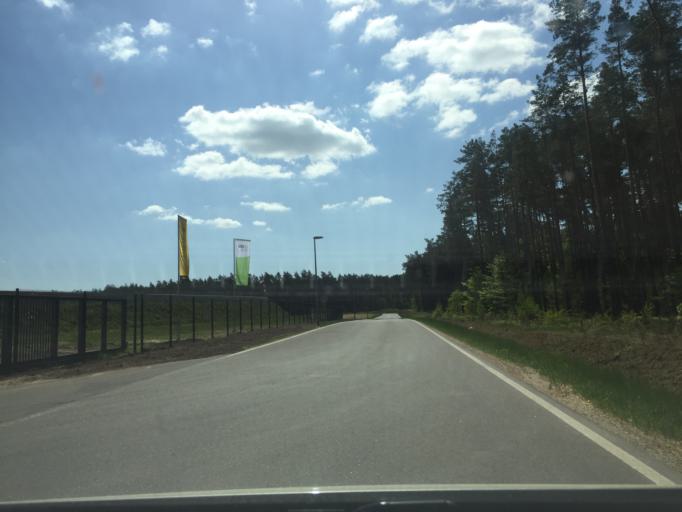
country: DE
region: Mecklenburg-Vorpommern
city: Torgelow
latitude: 53.6367
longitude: 13.9865
